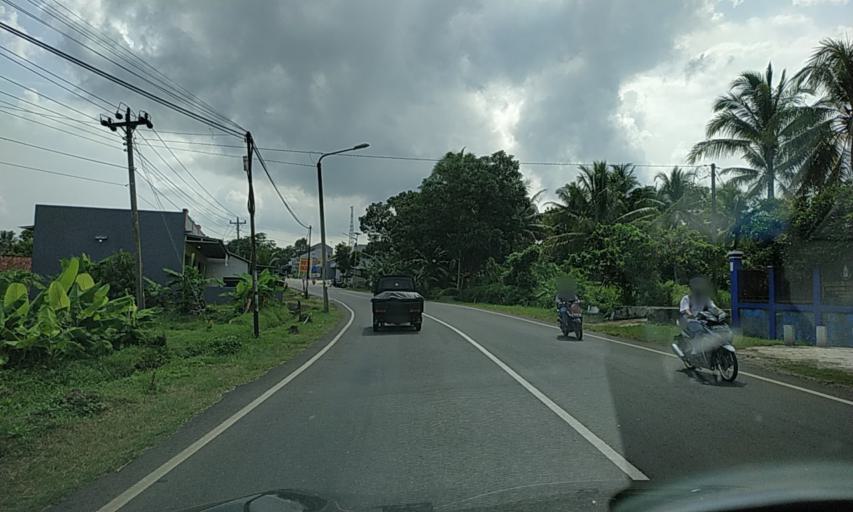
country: ID
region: Central Java
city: Cihandiwung Lor
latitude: -7.3356
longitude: 108.6936
